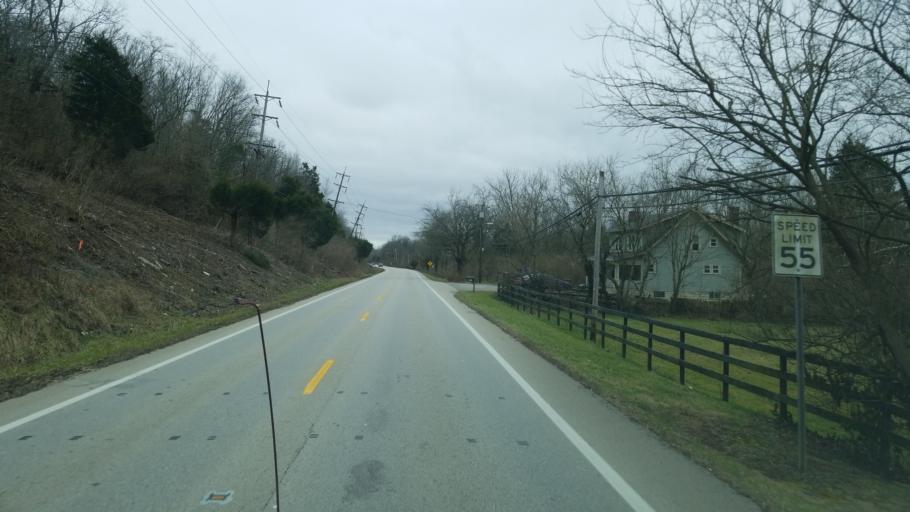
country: US
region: Ohio
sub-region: Clermont County
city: New Richmond
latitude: 38.9366
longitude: -84.2662
